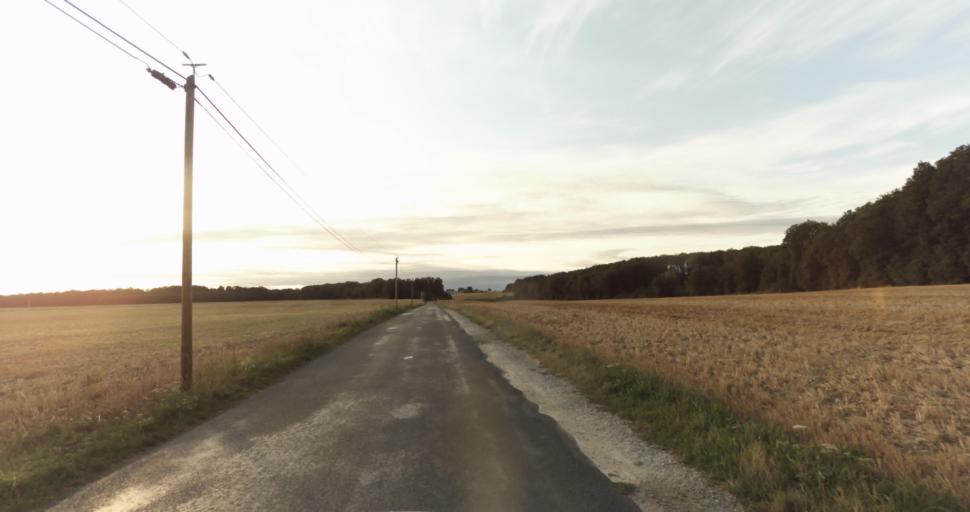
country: FR
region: Haute-Normandie
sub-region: Departement de l'Eure
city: Marcilly-sur-Eure
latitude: 48.8778
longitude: 1.2669
